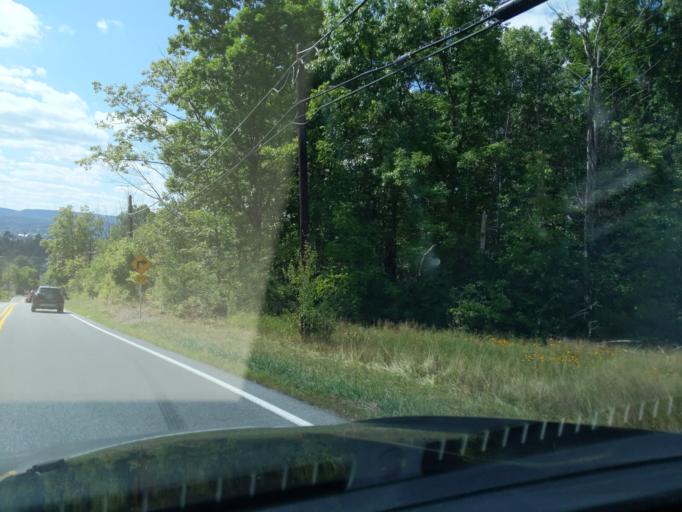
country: US
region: Pennsylvania
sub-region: Blair County
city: Greenwood
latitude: 40.5169
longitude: -78.3674
